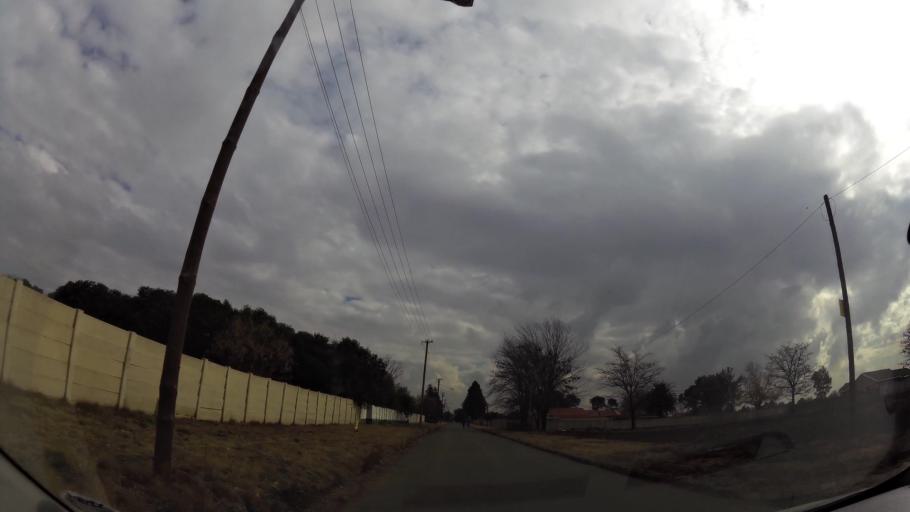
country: ZA
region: Gauteng
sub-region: Sedibeng District Municipality
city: Meyerton
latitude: -26.5987
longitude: 27.9997
